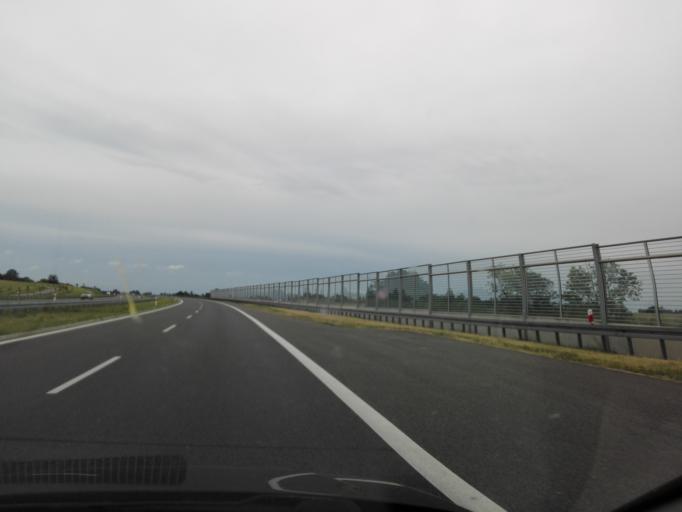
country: PL
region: Lublin Voivodeship
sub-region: Powiat lubelski
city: Jastkow
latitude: 51.2968
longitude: 22.4053
